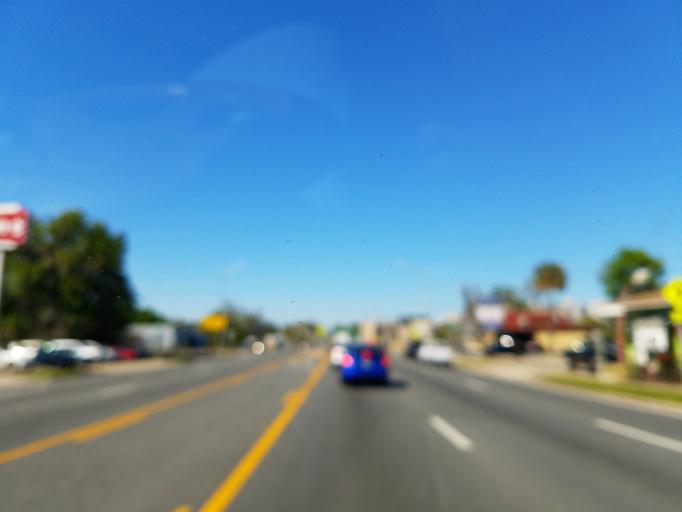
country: US
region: Florida
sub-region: Marion County
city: Ocala
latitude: 29.1842
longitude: -82.1404
